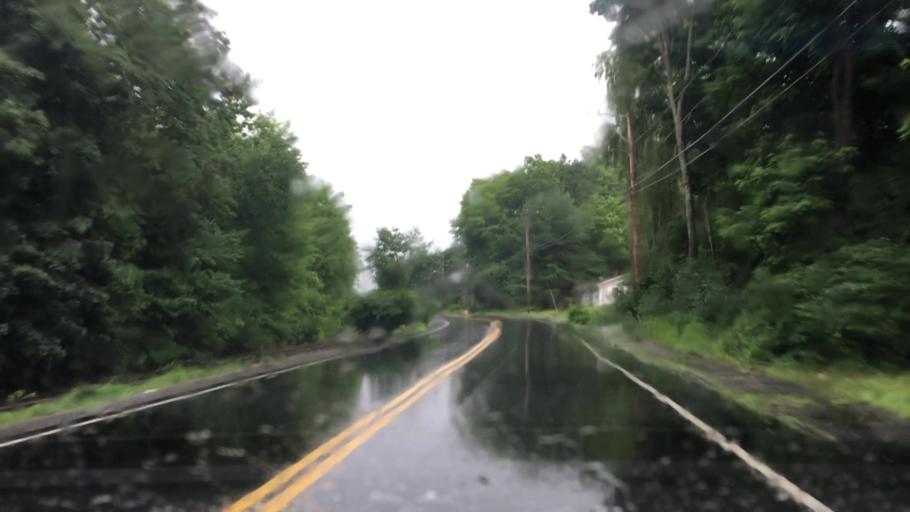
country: US
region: Maine
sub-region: Kennebec County
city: Randolph
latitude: 44.2228
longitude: -69.7652
